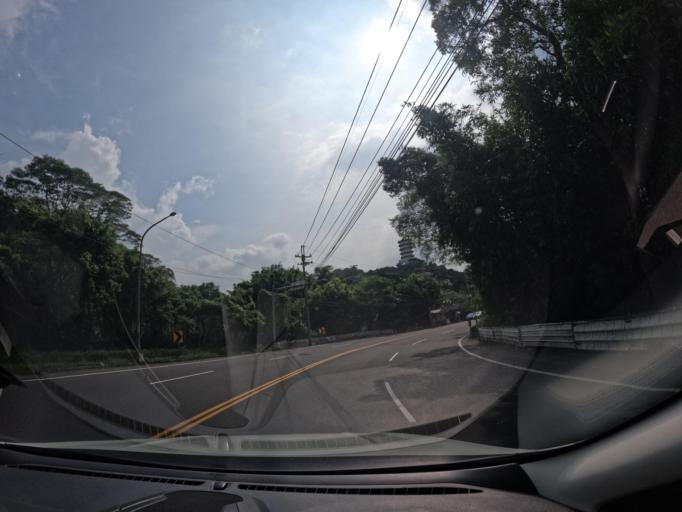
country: TW
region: Taiwan
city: Daxi
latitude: 24.9029
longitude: 121.3497
